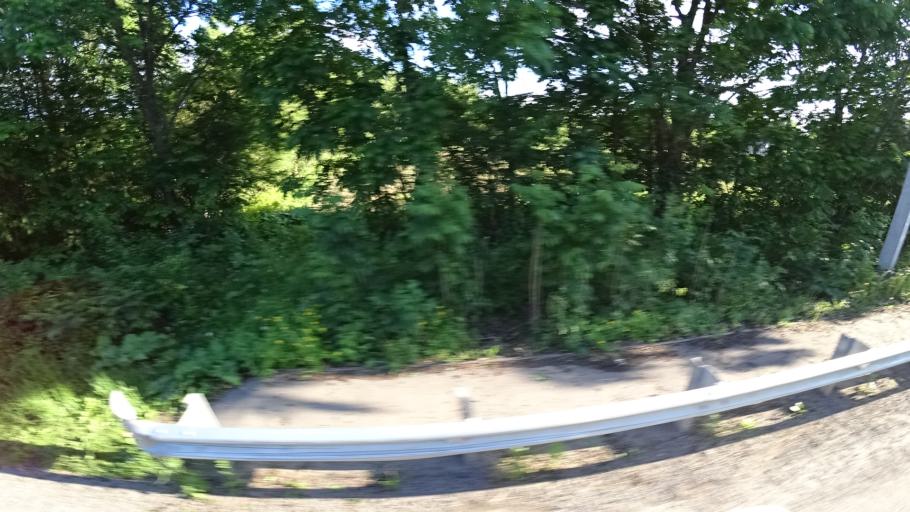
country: RU
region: Khabarovsk Krai
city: Khor
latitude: 47.8539
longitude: 134.9730
